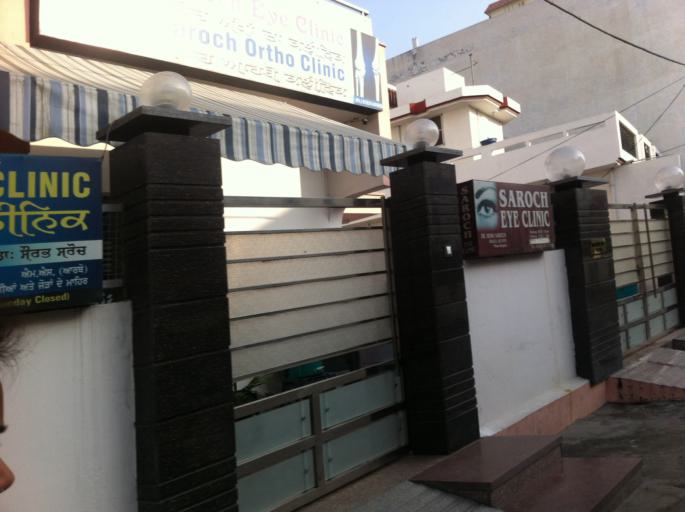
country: IN
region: Punjab
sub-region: Kapurthala
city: Phagwara
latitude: 31.2159
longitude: 75.7735
